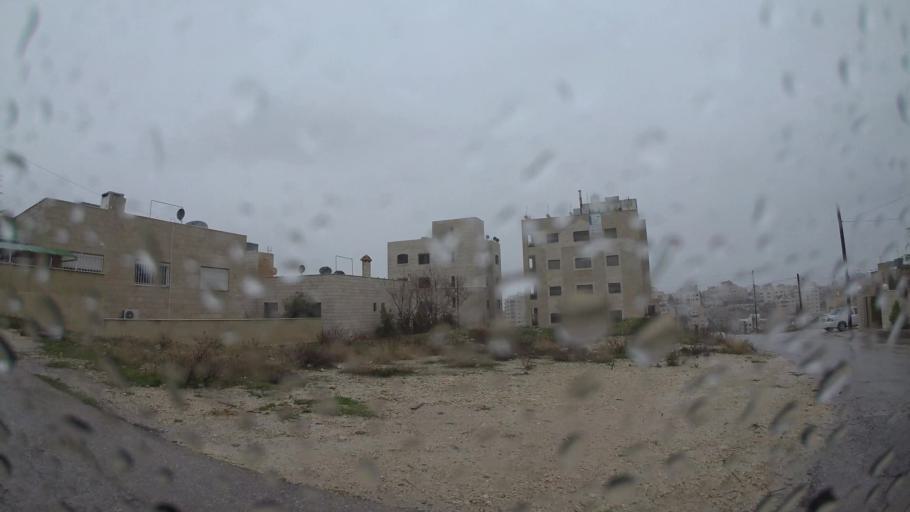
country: JO
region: Amman
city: Al Jubayhah
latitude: 32.0112
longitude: 35.8911
